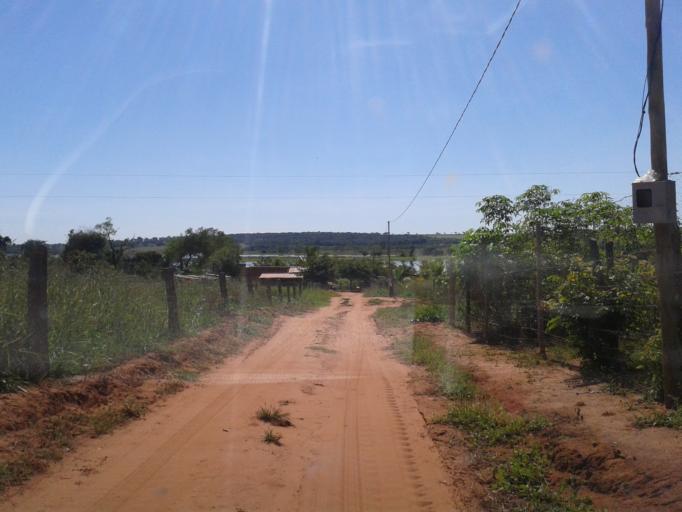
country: BR
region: Minas Gerais
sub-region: Santa Vitoria
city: Santa Vitoria
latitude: -19.0075
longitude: -50.3269
